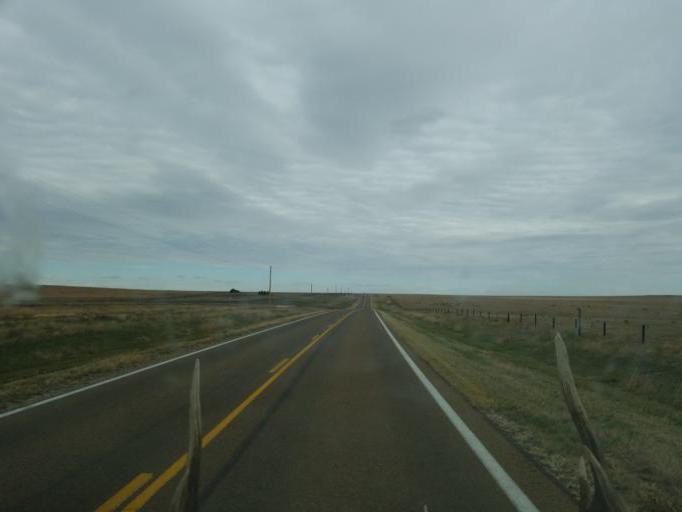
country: US
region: Kansas
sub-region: Wallace County
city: Sharon Springs
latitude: 38.9740
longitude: -101.4415
